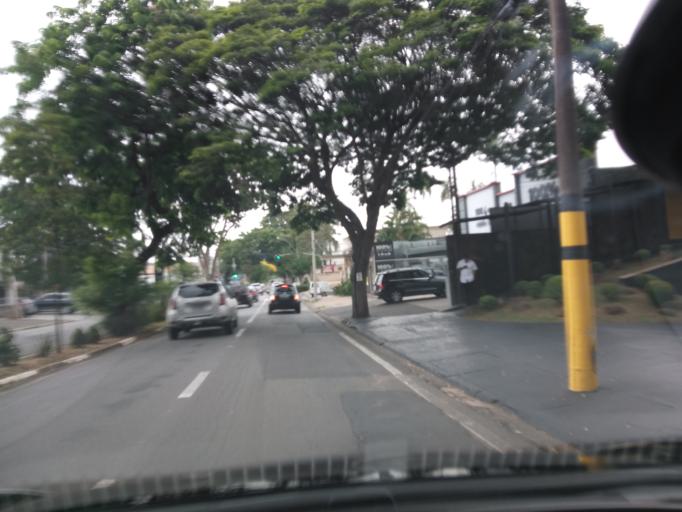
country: BR
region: Sao Paulo
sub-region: Campinas
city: Campinas
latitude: -22.8980
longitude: -47.0300
